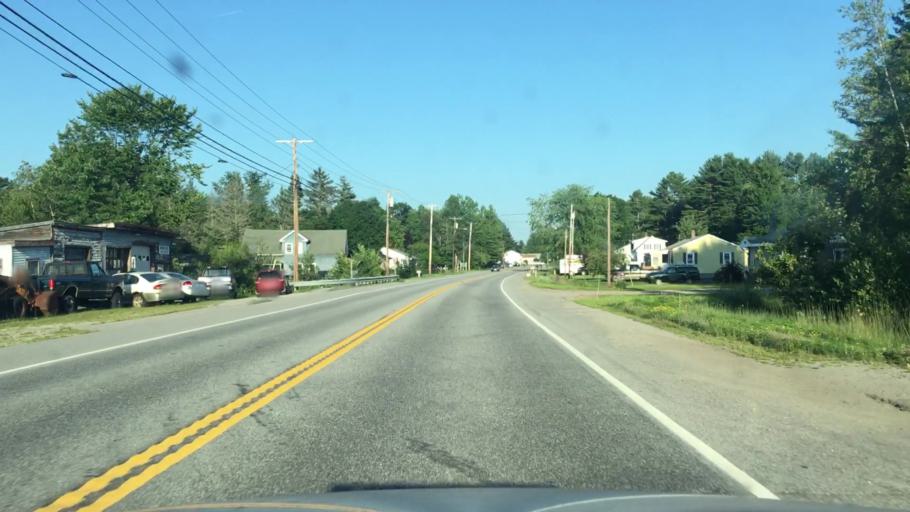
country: US
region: Maine
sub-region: Androscoggin County
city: Lisbon
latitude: 44.0504
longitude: -70.1285
